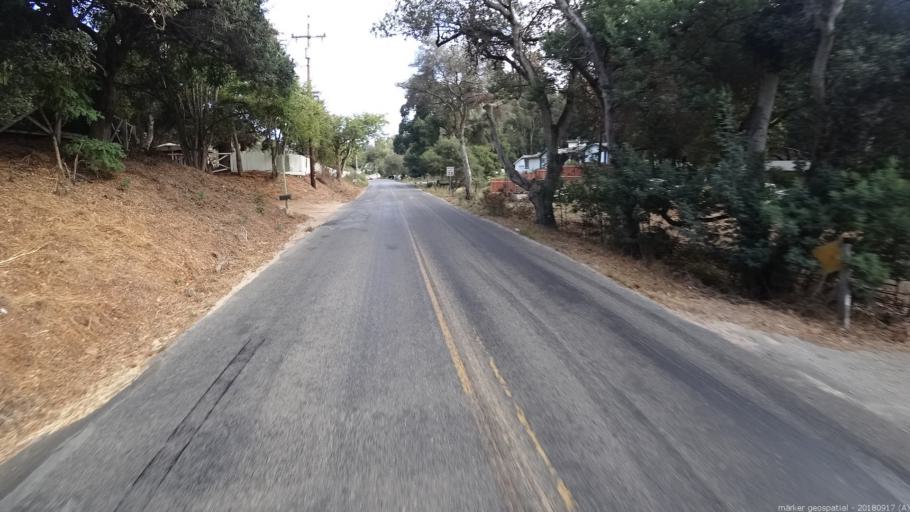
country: US
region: California
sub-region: Monterey County
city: Elkhorn
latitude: 36.8044
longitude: -121.7037
